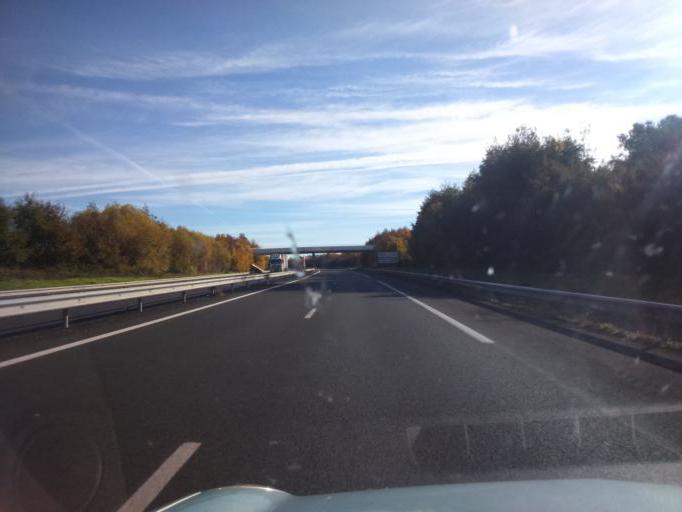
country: FR
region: Poitou-Charentes
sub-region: Departement de la Charente-Maritime
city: Tonnay-Charente
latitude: 45.9546
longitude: -0.9016
